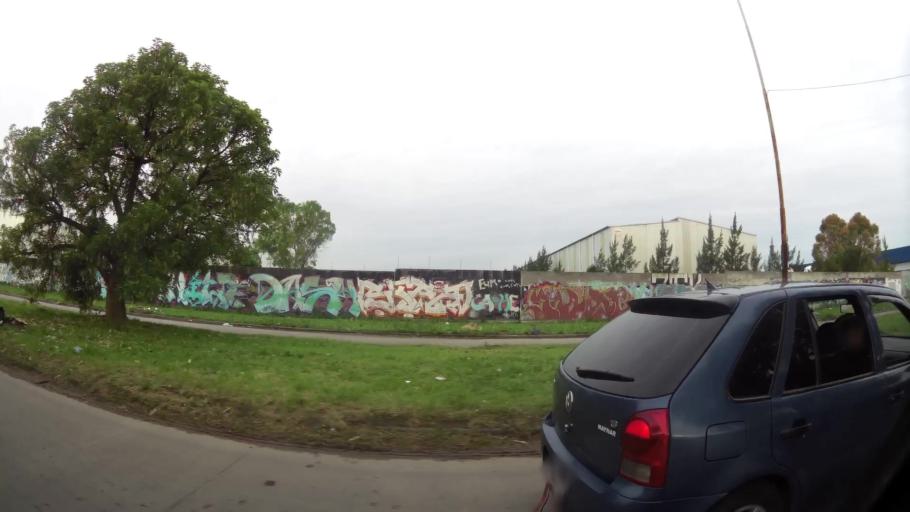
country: AR
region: Buenos Aires
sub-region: Partido de Lanus
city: Lanus
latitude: -34.7379
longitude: -58.3440
